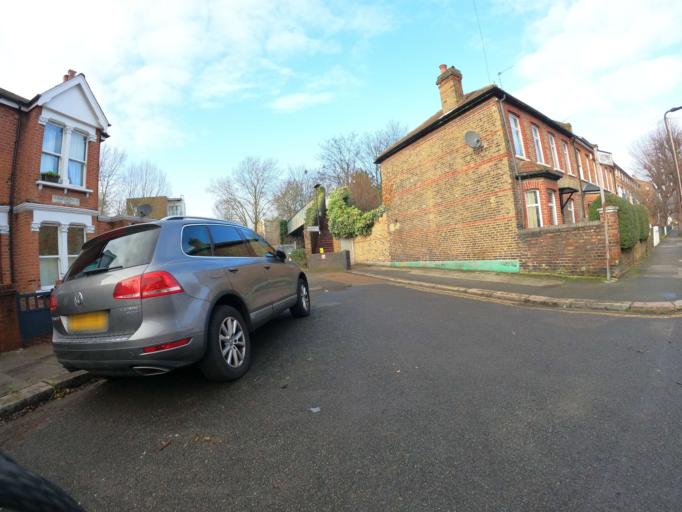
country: GB
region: England
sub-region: Greater London
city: Acton
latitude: 51.5006
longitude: -0.2680
